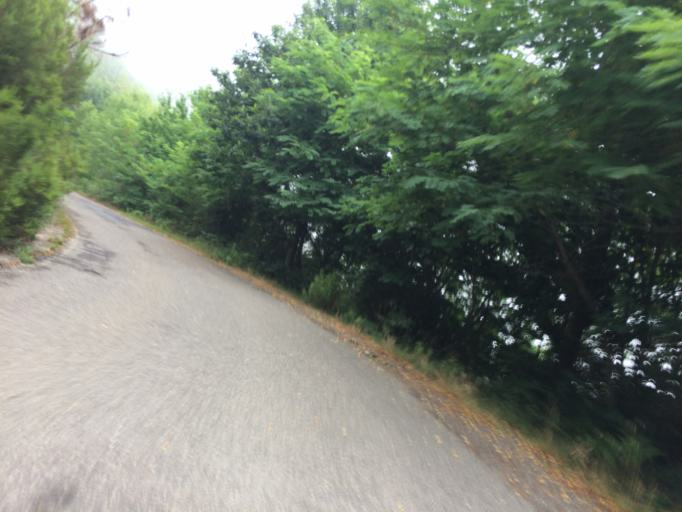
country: IT
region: Liguria
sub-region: Provincia di Imperia
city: Ceriana
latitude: 43.8549
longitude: 7.7421
